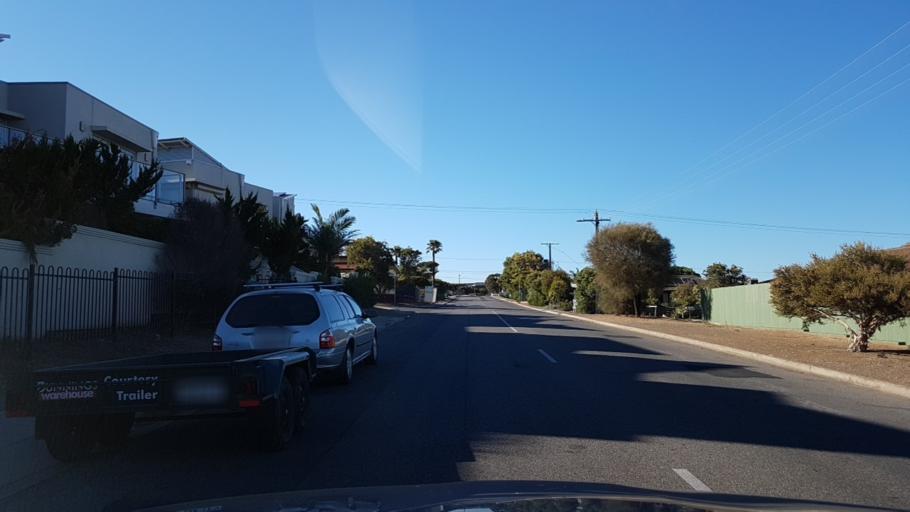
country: AU
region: South Australia
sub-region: Adelaide
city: Port Noarlunga
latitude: -35.1326
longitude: 138.4733
